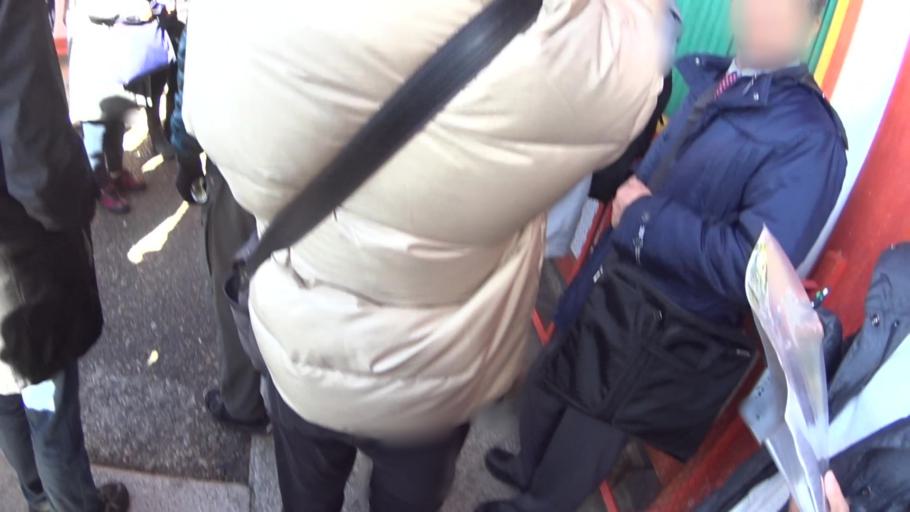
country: JP
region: Kyoto
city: Kyoto
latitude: 35.0031
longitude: 135.7824
